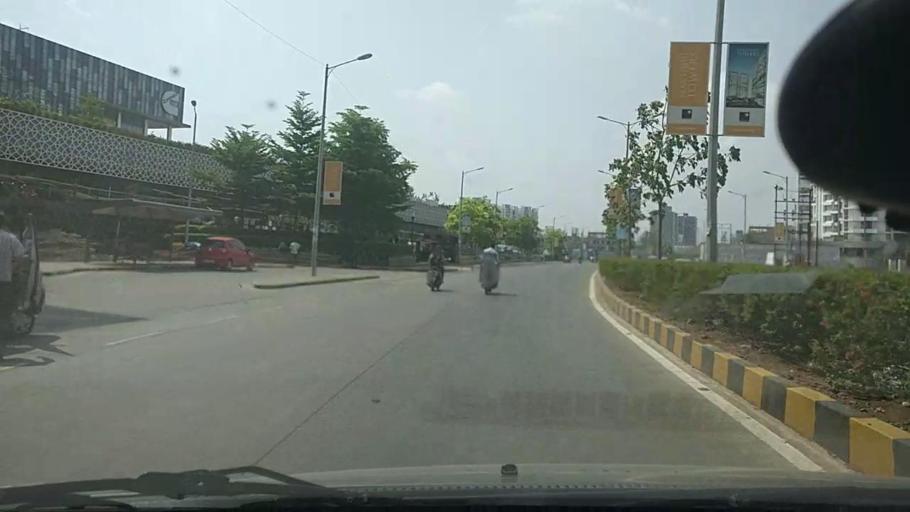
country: IN
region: Maharashtra
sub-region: Pune Division
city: Pimpri
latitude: 18.5689
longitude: 73.7751
